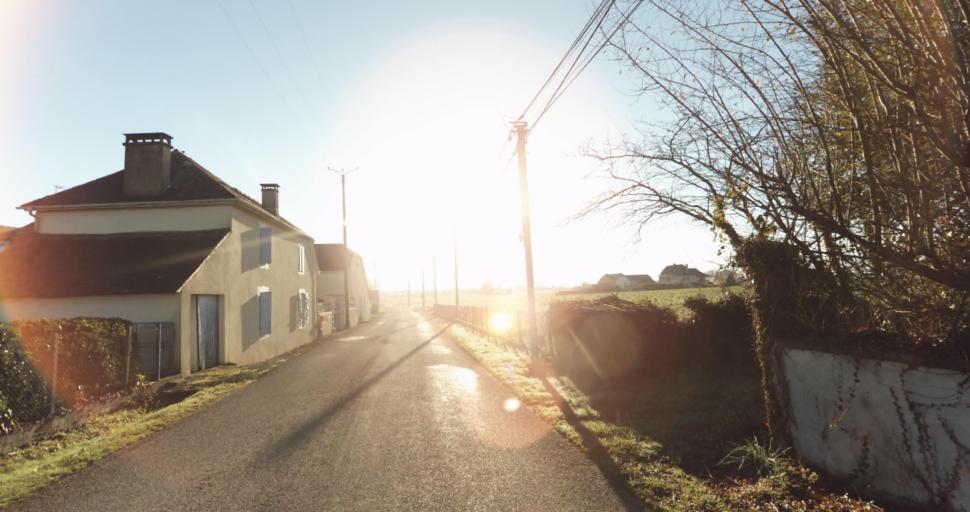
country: FR
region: Aquitaine
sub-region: Departement des Pyrenees-Atlantiques
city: Morlaas
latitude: 43.3224
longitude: -0.2523
